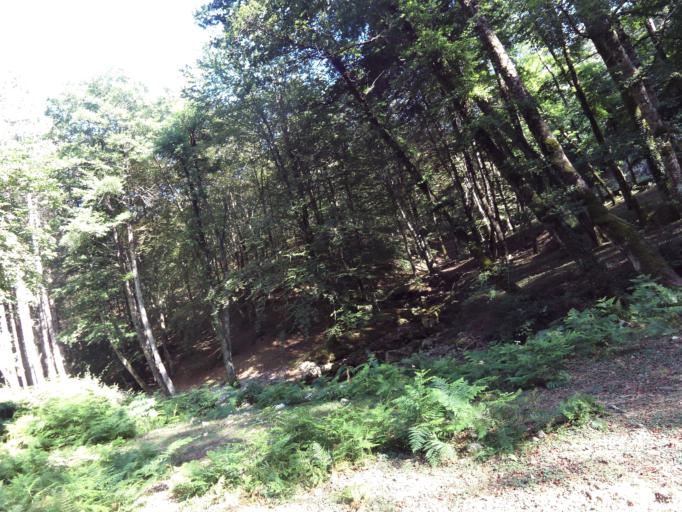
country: IT
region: Calabria
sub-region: Provincia di Vibo-Valentia
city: Nardodipace
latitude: 38.5037
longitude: 16.3755
